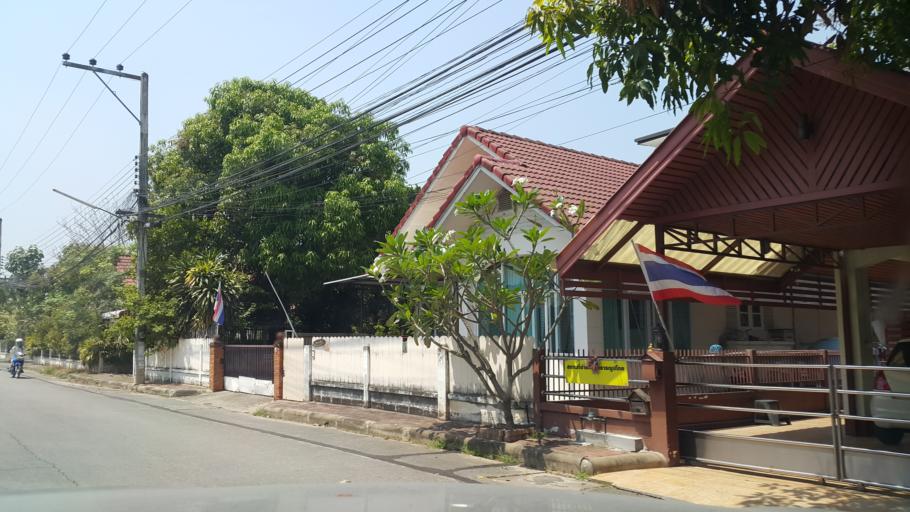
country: TH
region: Chiang Mai
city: Chiang Mai
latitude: 18.7571
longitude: 98.9926
